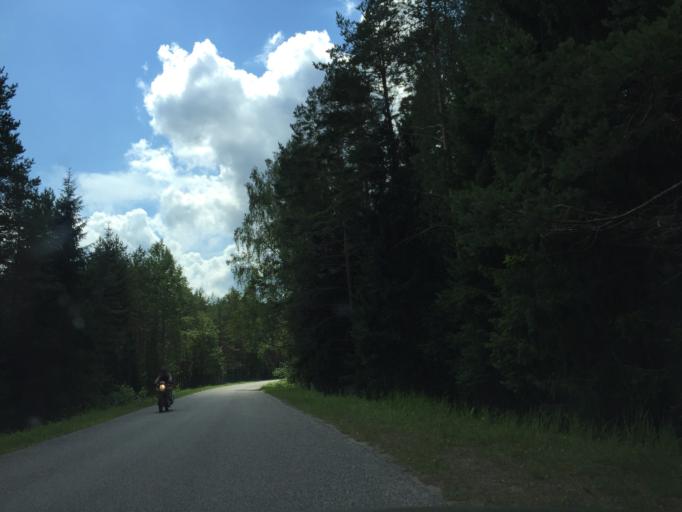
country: LV
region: Ligatne
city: Ligatne
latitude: 57.2466
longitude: 25.0680
